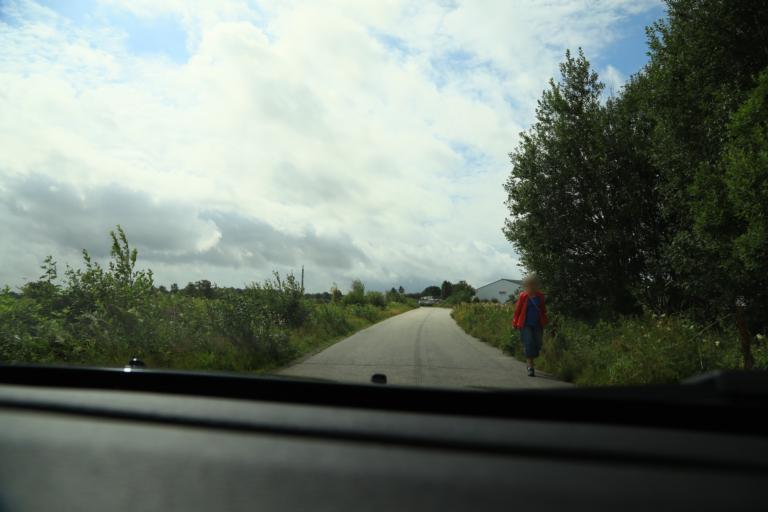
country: SE
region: Halland
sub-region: Varbergs Kommun
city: Traslovslage
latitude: 57.1147
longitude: 12.3092
